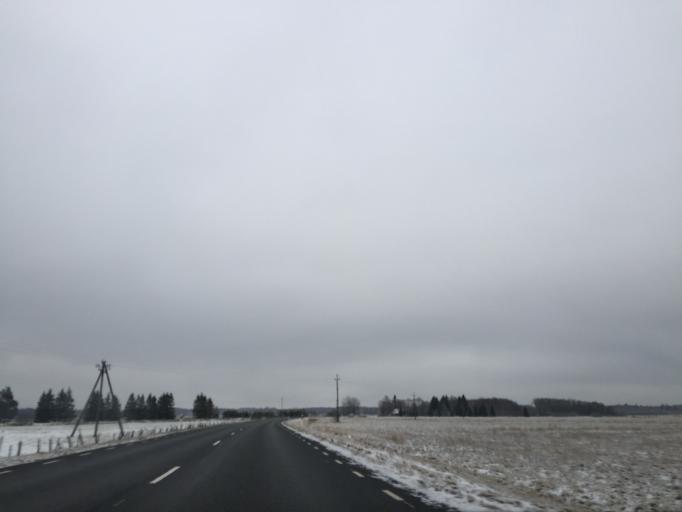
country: EE
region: Laeaene
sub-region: Lihula vald
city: Lihula
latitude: 58.6696
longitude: 23.8294
